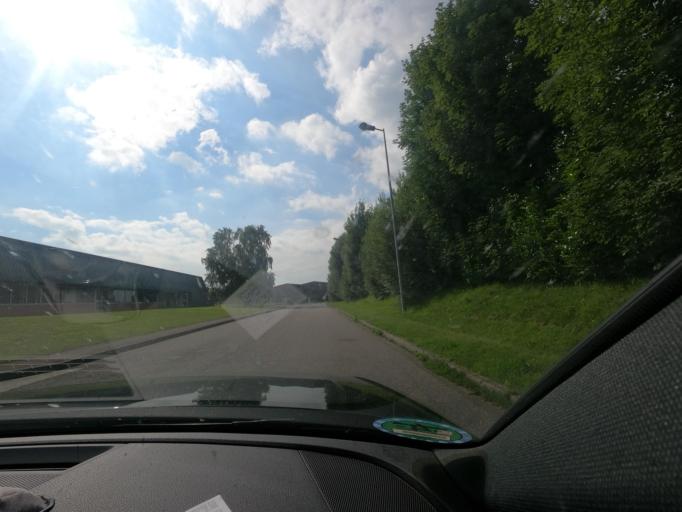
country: FR
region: Lower Normandy
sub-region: Departement du Calvados
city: La Riviere-Saint-Sauveur
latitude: 49.3948
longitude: 0.2577
